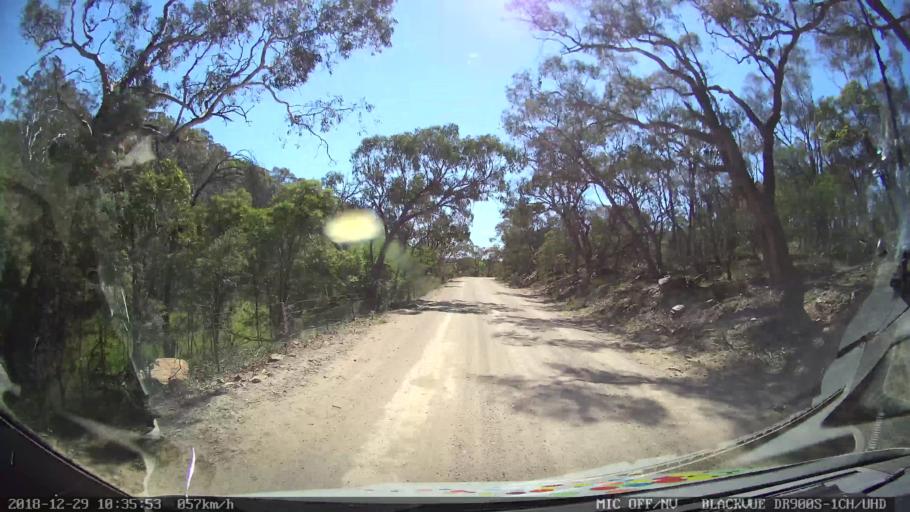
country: AU
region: New South Wales
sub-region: Yass Valley
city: Gundaroo
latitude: -34.9928
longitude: 149.4863
